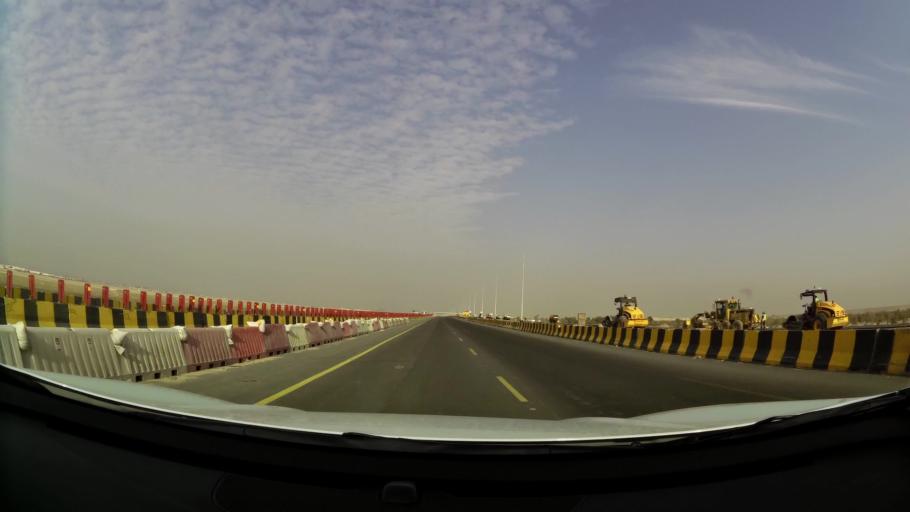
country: AE
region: Abu Dhabi
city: Abu Dhabi
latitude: 24.2732
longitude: 54.5092
